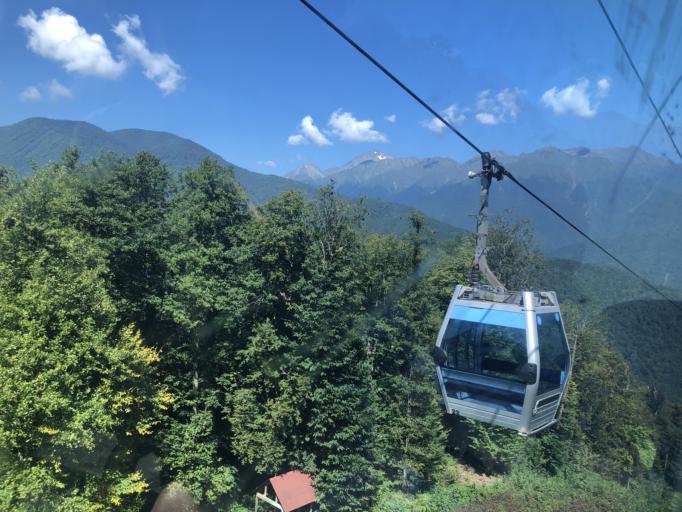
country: RU
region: Krasnodarskiy
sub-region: Sochi City
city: Krasnaya Polyana
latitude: 43.6742
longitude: 40.2620
